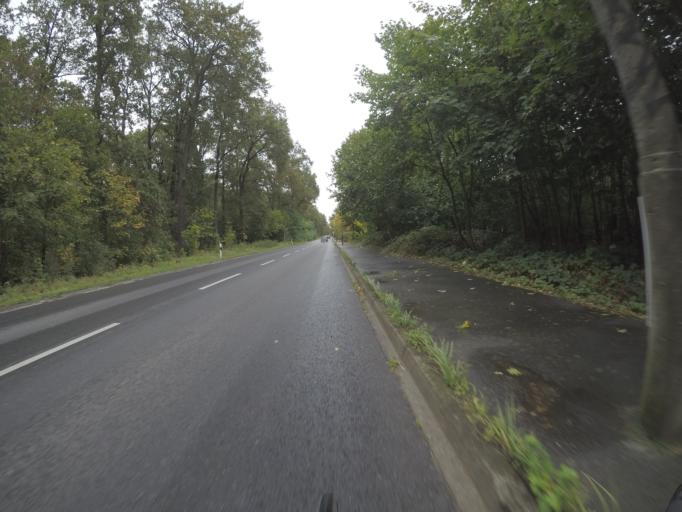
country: DE
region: Berlin
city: Buch
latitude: 52.6391
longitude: 13.4744
